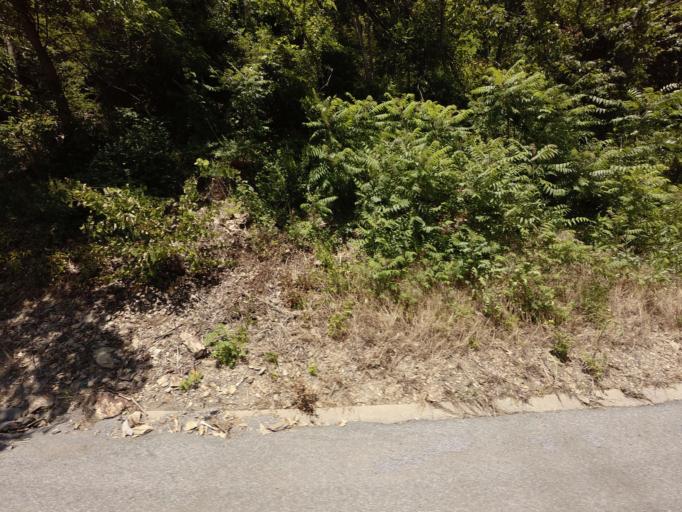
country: US
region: West Virginia
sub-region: Jefferson County
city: Bolivar
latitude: 39.3201
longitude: -77.7496
